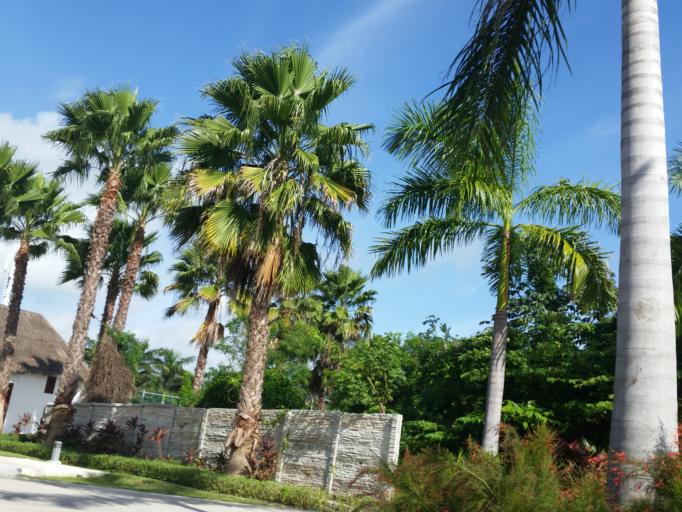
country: MX
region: Quintana Roo
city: Playa del Carmen
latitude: 20.6739
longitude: -87.0338
